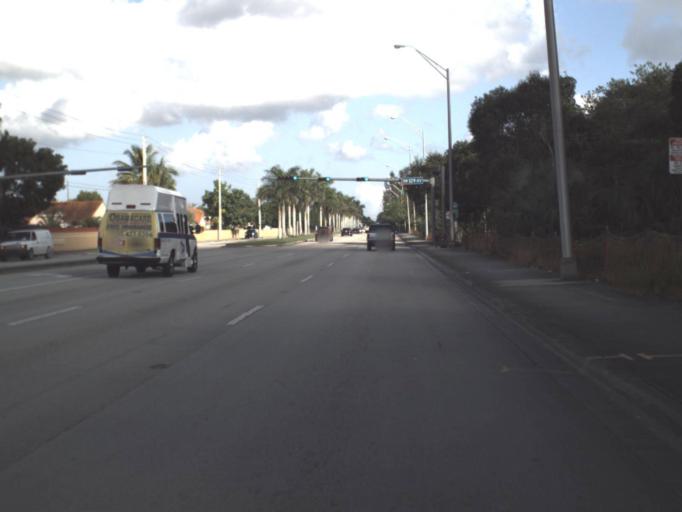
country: US
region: Florida
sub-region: Miami-Dade County
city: Three Lakes
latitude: 25.6265
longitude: -80.4008
